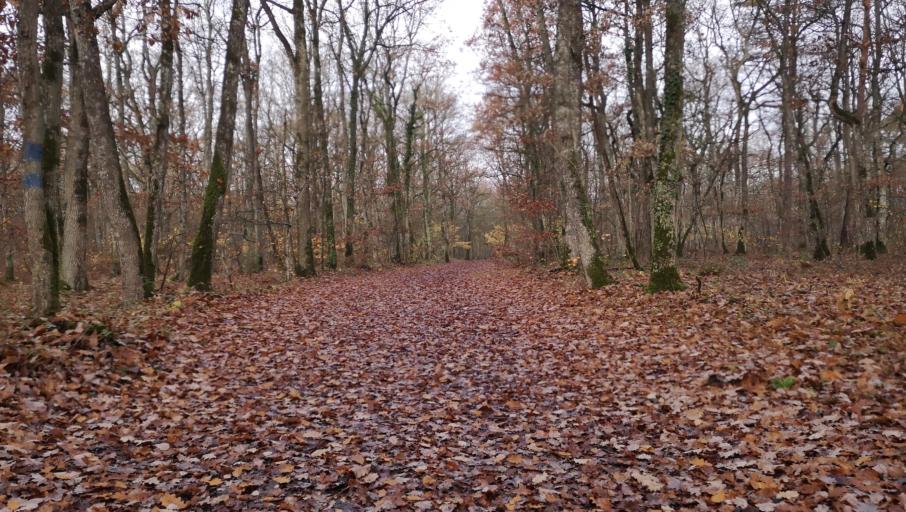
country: FR
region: Centre
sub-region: Departement du Loiret
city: Semoy
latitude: 47.9398
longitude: 1.9708
